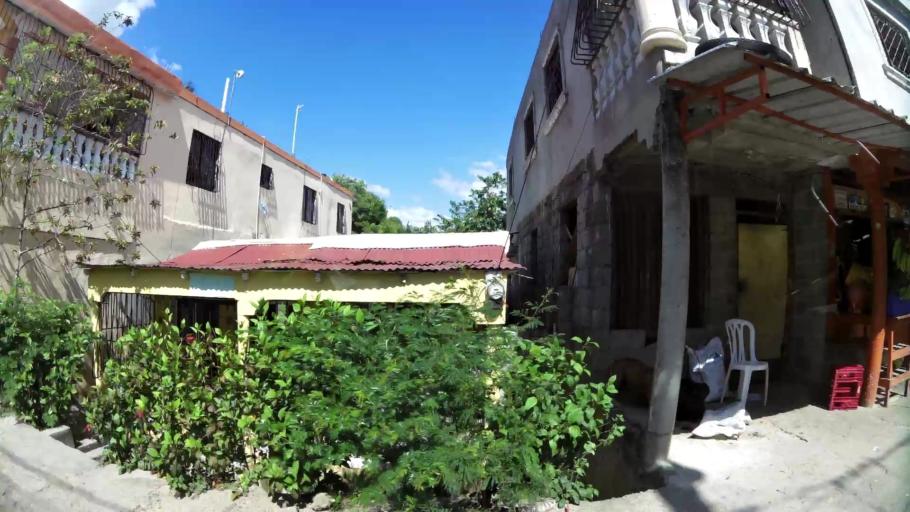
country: DO
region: San Cristobal
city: San Cristobal
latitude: 18.4242
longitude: -70.0830
